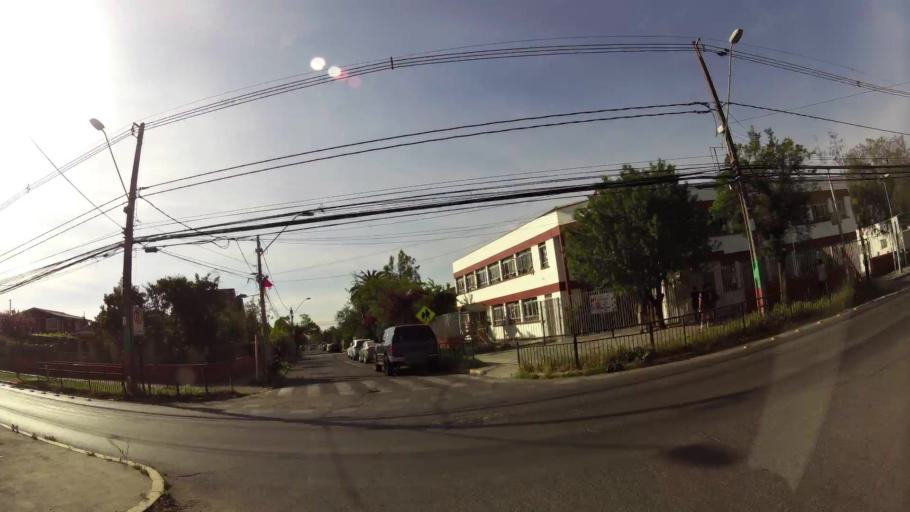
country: CL
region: Santiago Metropolitan
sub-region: Provincia de Santiago
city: La Pintana
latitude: -33.5398
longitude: -70.5791
